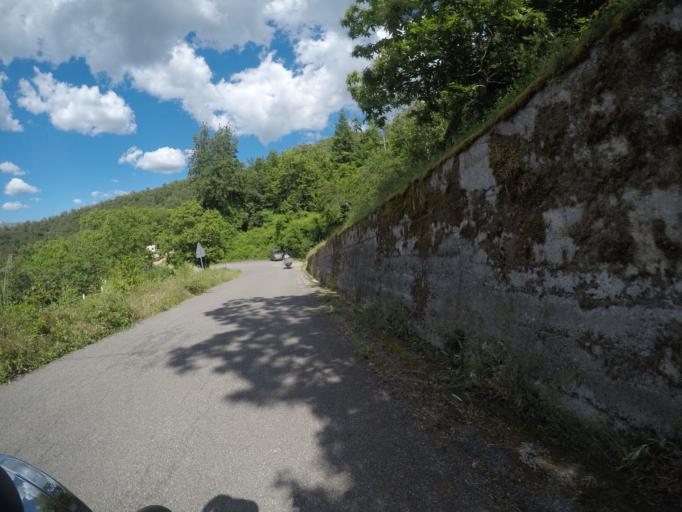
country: IT
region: Tuscany
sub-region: Provincia di Massa-Carrara
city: Casola in Lunigiana
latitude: 44.1811
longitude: 10.1579
